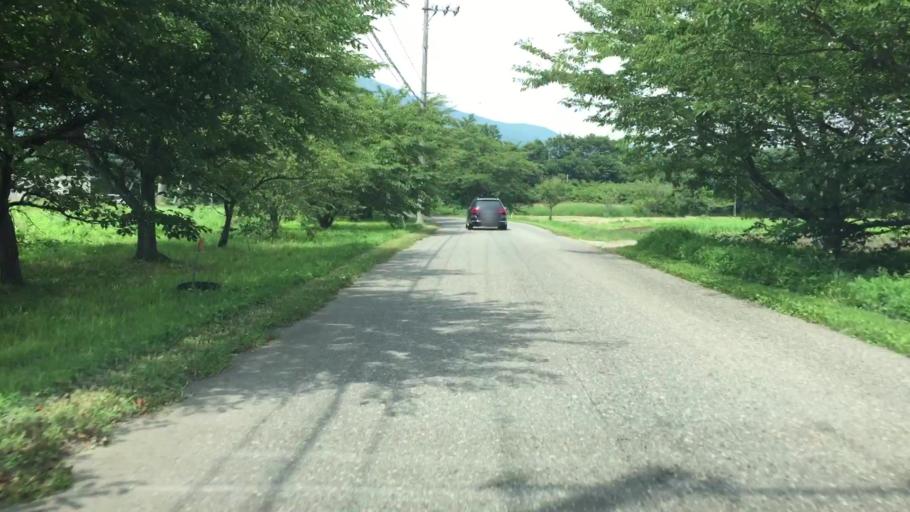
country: JP
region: Tochigi
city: Kuroiso
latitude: 37.0416
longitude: 139.9526
